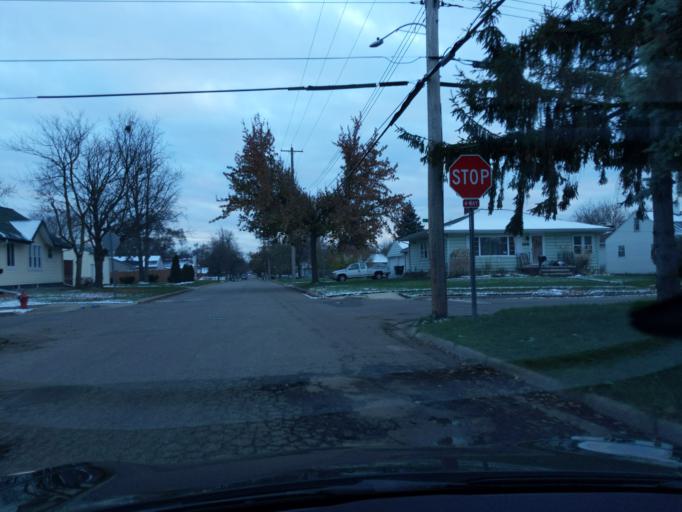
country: US
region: Michigan
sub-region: Ingham County
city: Lansing
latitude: 42.7623
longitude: -84.5407
